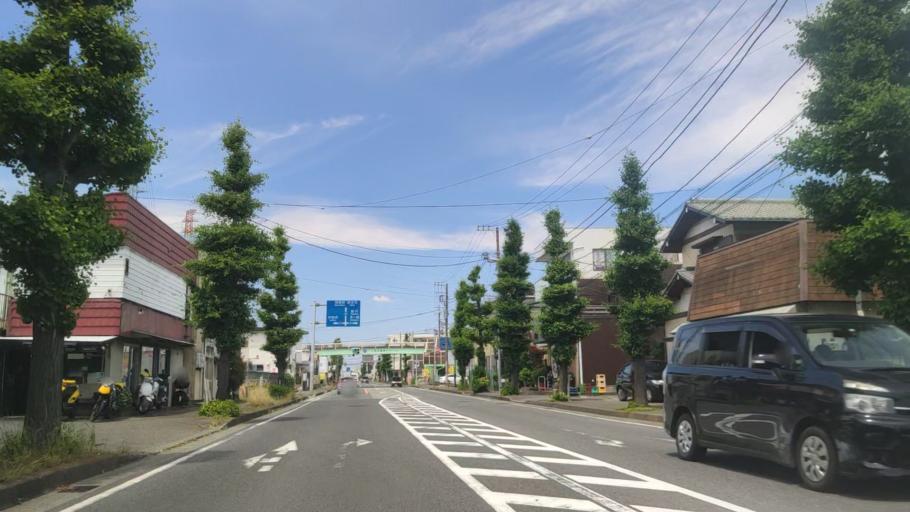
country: JP
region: Kanagawa
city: Chigasaki
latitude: 35.3637
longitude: 139.3810
